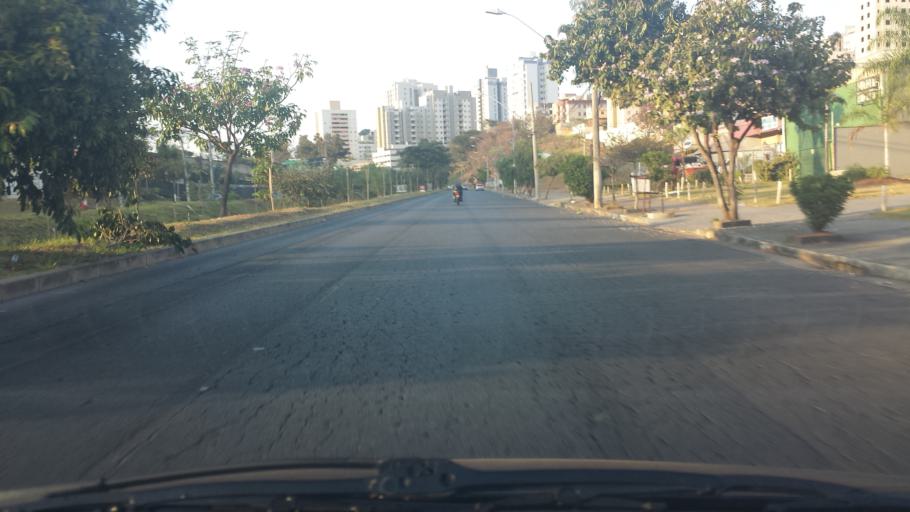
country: BR
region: Minas Gerais
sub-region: Belo Horizonte
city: Belo Horizonte
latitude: -19.8840
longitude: -43.9936
